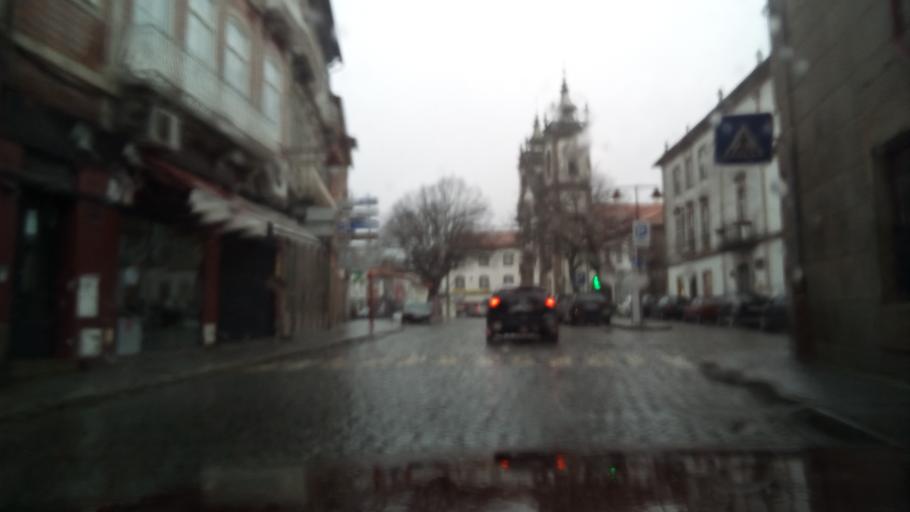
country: PT
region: Guarda
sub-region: Guarda
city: Guarda
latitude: 40.5378
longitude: -7.2678
